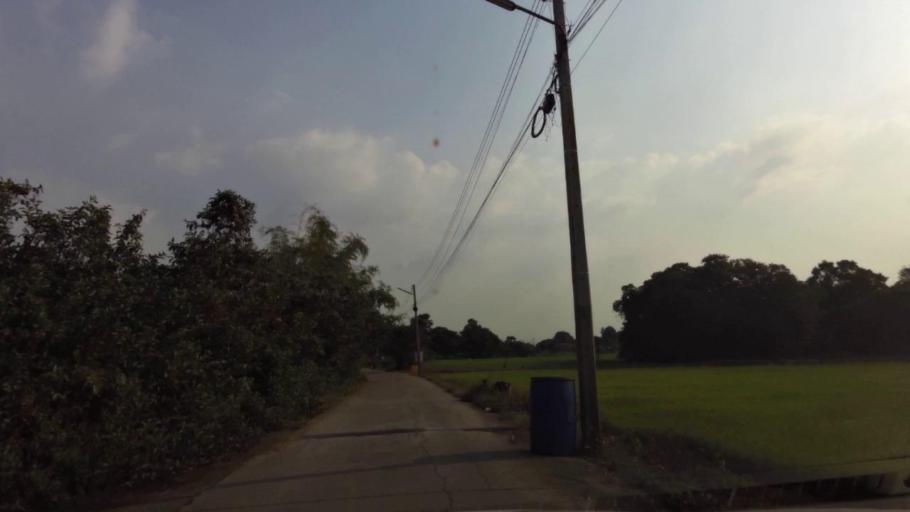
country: TH
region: Phra Nakhon Si Ayutthaya
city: Phra Nakhon Si Ayutthaya
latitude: 14.3279
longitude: 100.5670
